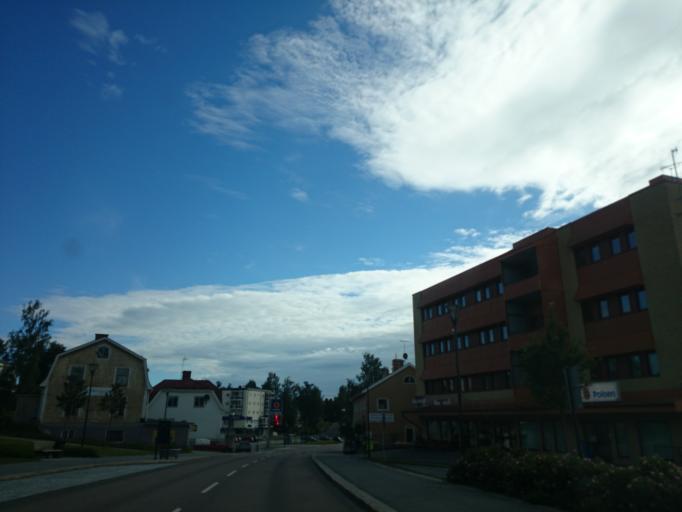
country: SE
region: Vaesternorrland
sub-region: Timra Kommun
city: Timra
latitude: 62.4885
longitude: 17.3273
